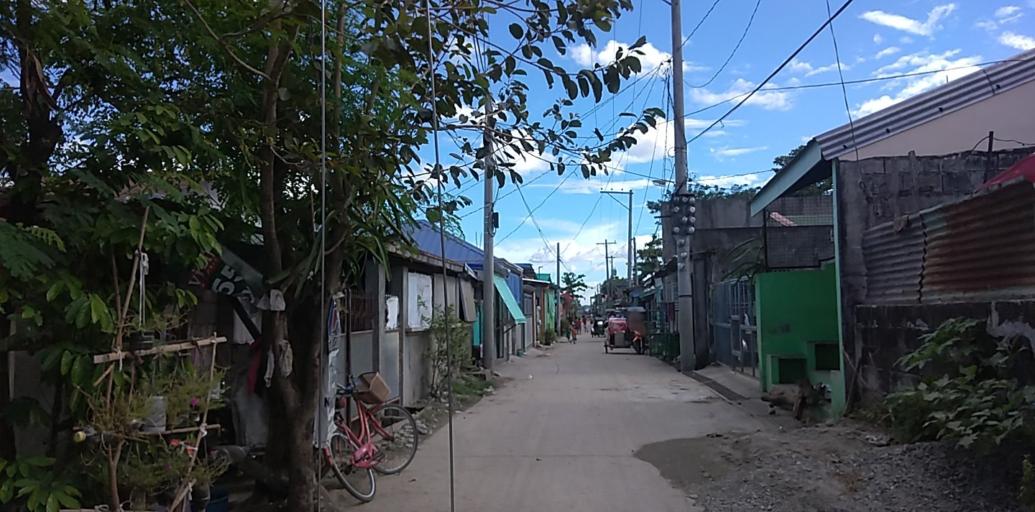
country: PH
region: Central Luzon
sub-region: Province of Pampanga
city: Arayat
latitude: 15.1377
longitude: 120.7706
